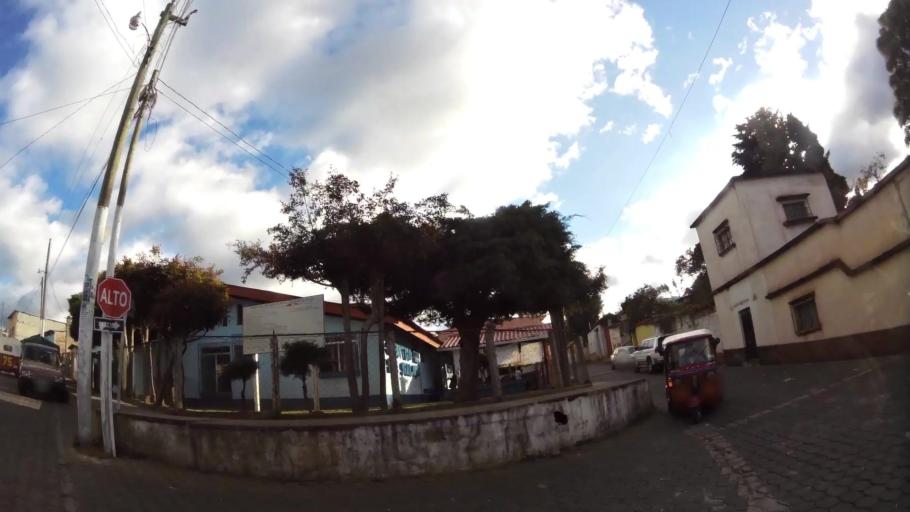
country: GT
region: Quiche
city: Chichicastenango
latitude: 14.9475
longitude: -91.1121
